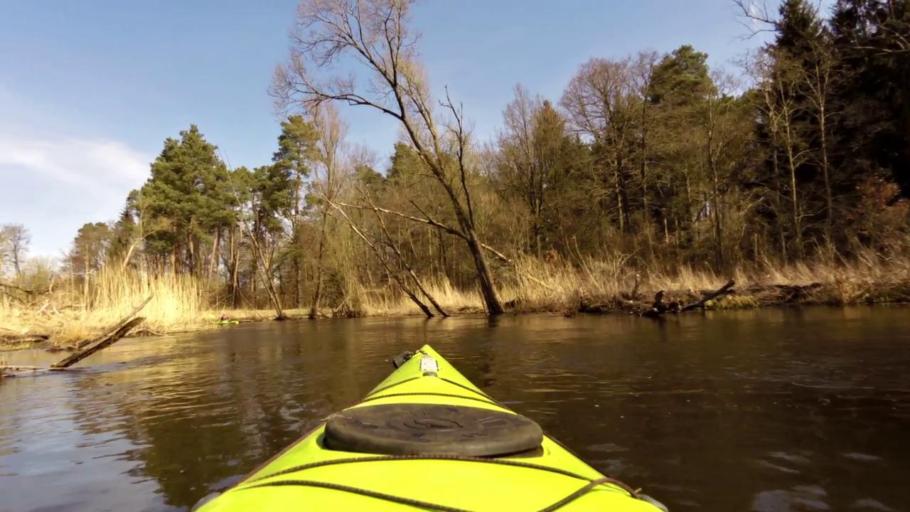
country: PL
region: West Pomeranian Voivodeship
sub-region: Powiat lobeski
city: Lobez
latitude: 53.6468
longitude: 15.5715
